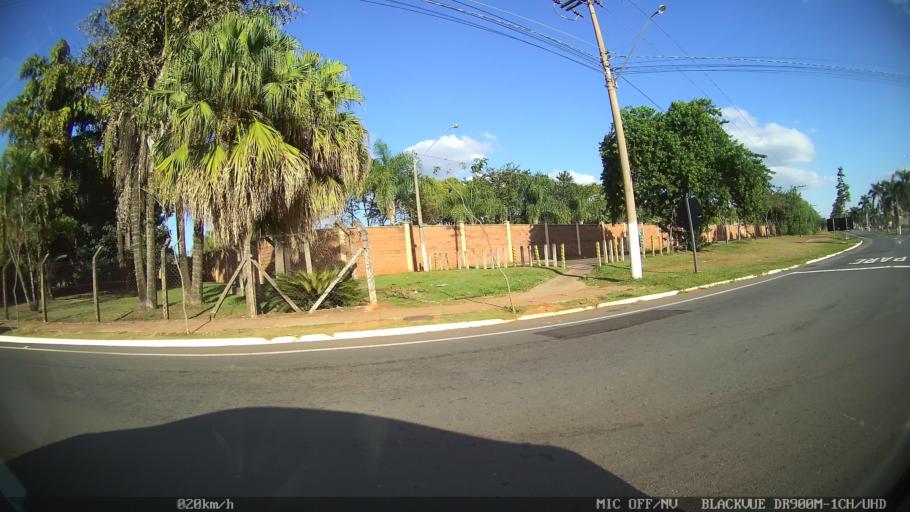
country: BR
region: Sao Paulo
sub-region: Santa Barbara D'Oeste
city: Santa Barbara d'Oeste
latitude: -22.7565
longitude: -47.4309
